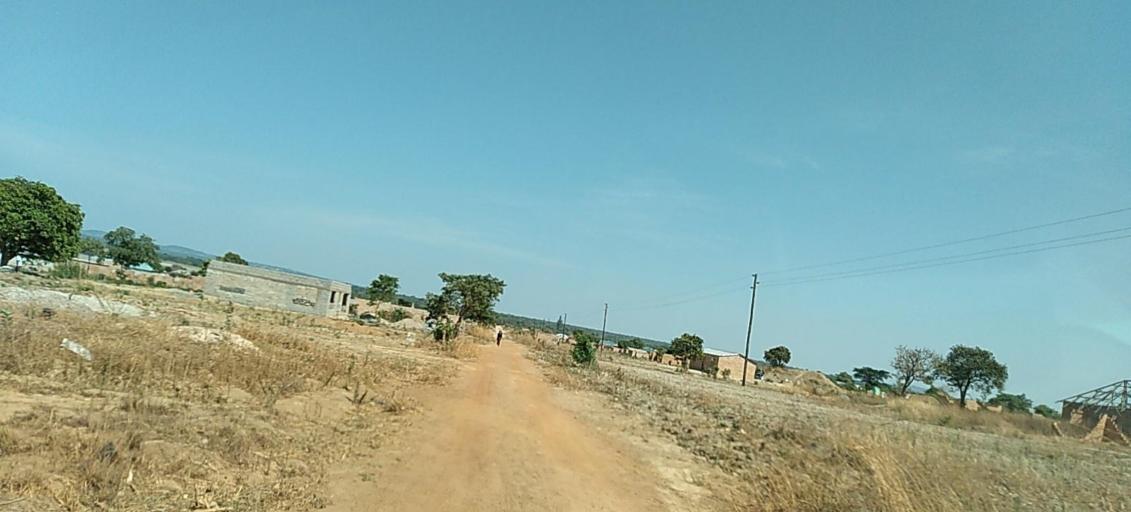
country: ZM
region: Copperbelt
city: Chililabombwe
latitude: -12.3405
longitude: 27.8691
